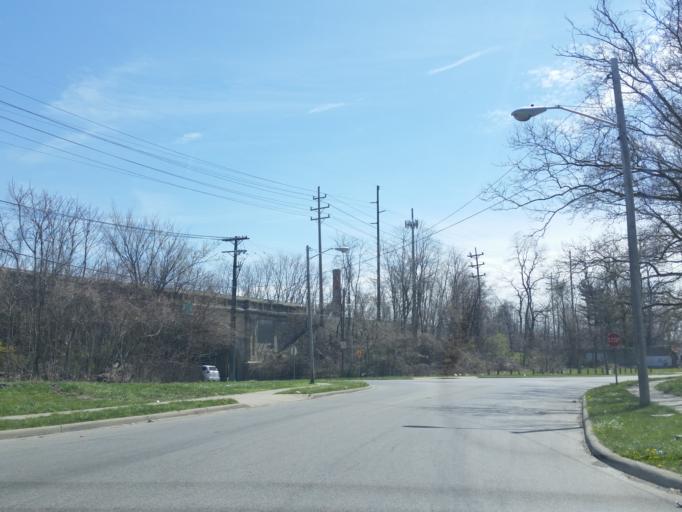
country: US
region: Ohio
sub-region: Cuyahoga County
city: East Cleveland
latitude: 41.5282
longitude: -81.5919
